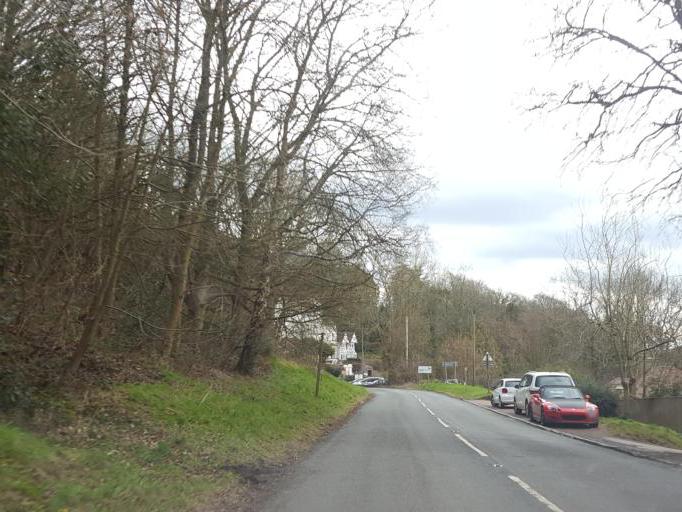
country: GB
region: England
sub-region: Worcestershire
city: Great Malvern
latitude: 52.0974
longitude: -2.3408
